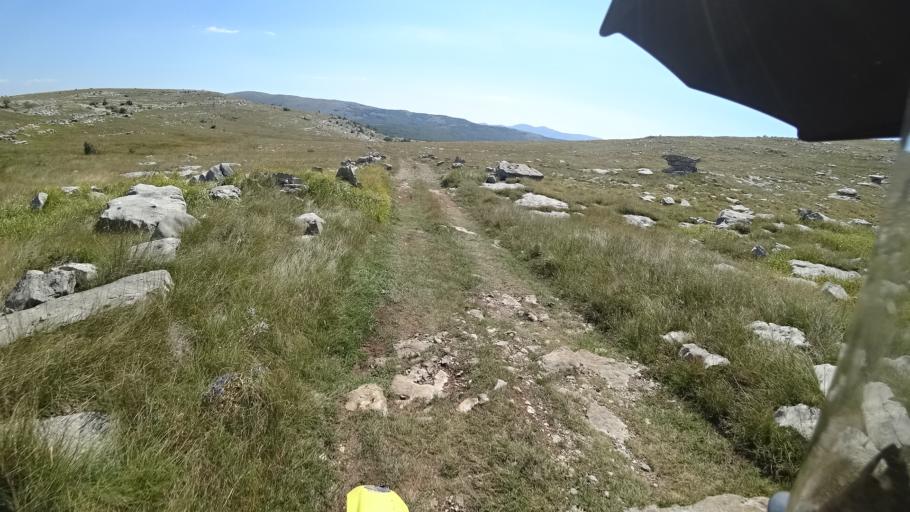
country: HR
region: Splitsko-Dalmatinska
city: Hrvace
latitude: 43.8995
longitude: 16.5899
